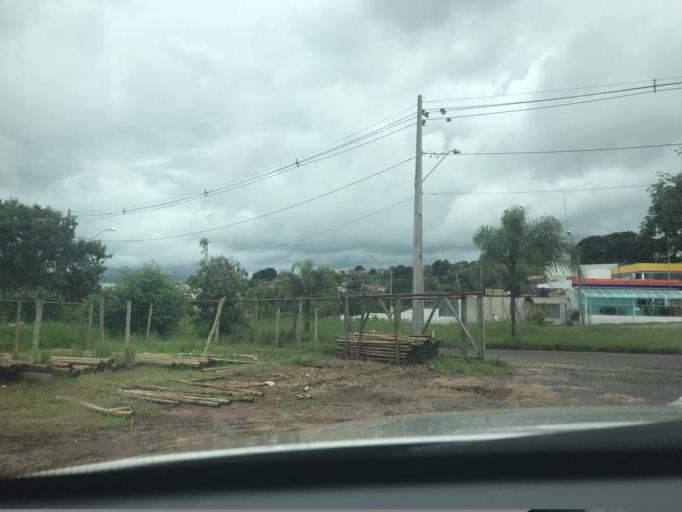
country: BR
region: Minas Gerais
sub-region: Araxa
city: Araxa
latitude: -19.5825
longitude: -46.9430
